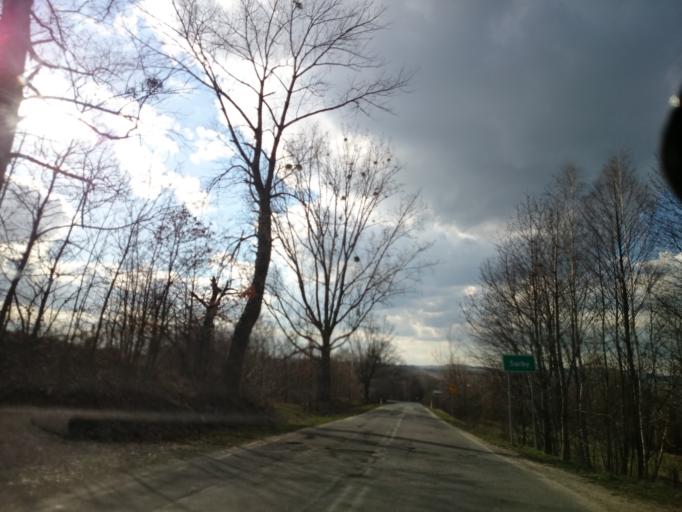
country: PL
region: Lower Silesian Voivodeship
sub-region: Powiat strzelinski
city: Przeworno
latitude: 50.6446
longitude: 17.1782
